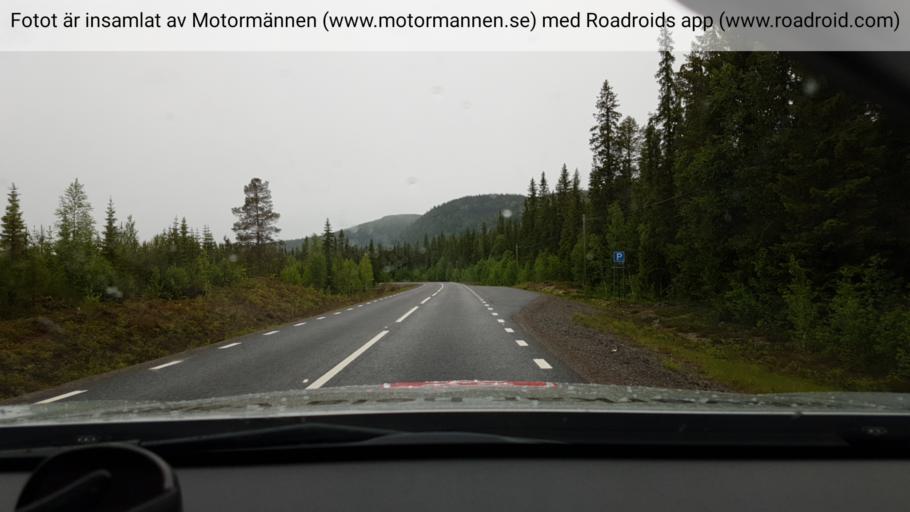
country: SE
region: Vaesterbotten
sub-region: Sorsele Kommun
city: Sorsele
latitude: 65.8005
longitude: 16.9604
